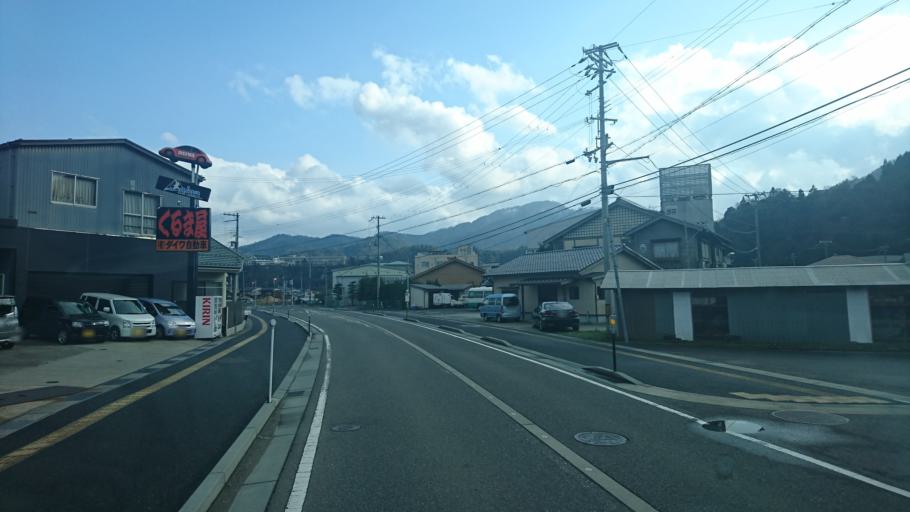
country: JP
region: Tottori
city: Tottori
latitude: 35.6245
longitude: 134.4455
